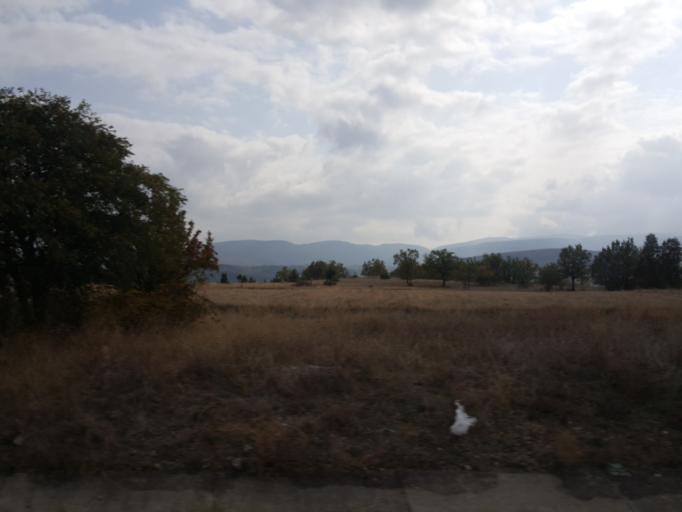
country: TR
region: Sinop
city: Sarayduzu
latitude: 41.3297
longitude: 34.7703
